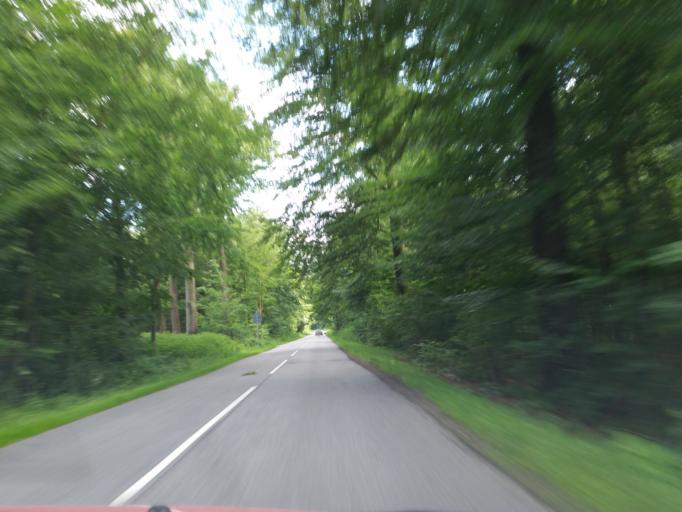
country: DK
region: South Denmark
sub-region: Vejle Kommune
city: Borkop
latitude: 55.6836
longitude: 9.6153
